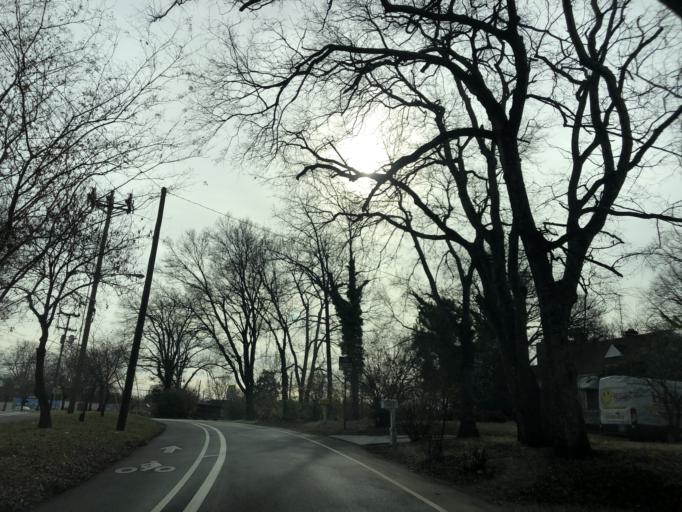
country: US
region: Tennessee
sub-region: Davidson County
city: Nashville
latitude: 36.2058
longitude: -86.7246
